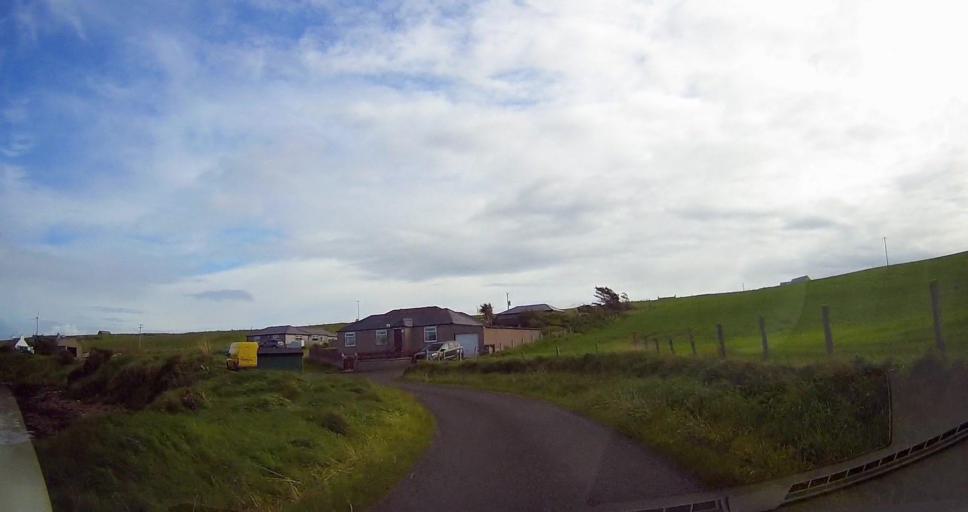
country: GB
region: Scotland
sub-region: Orkney Islands
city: Stromness
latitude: 58.7820
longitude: -3.2352
